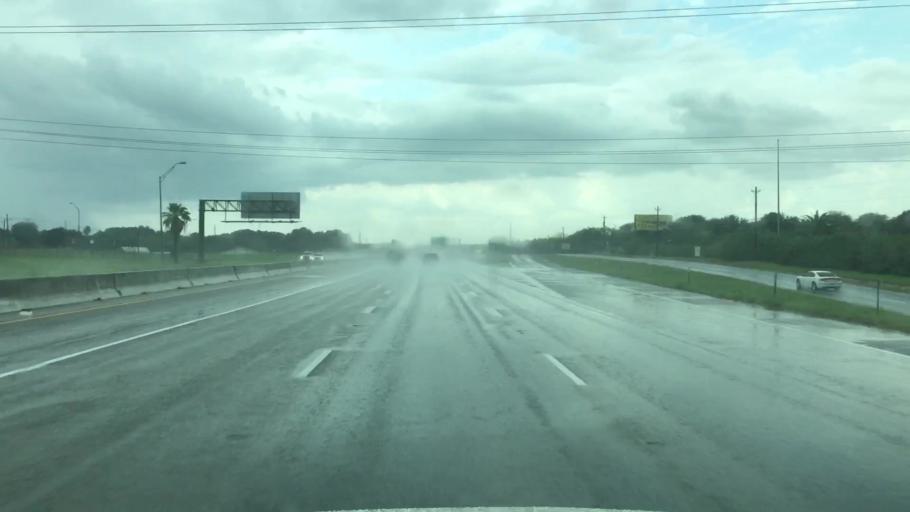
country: US
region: Texas
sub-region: Nueces County
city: Robstown
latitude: 27.8579
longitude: -97.6045
